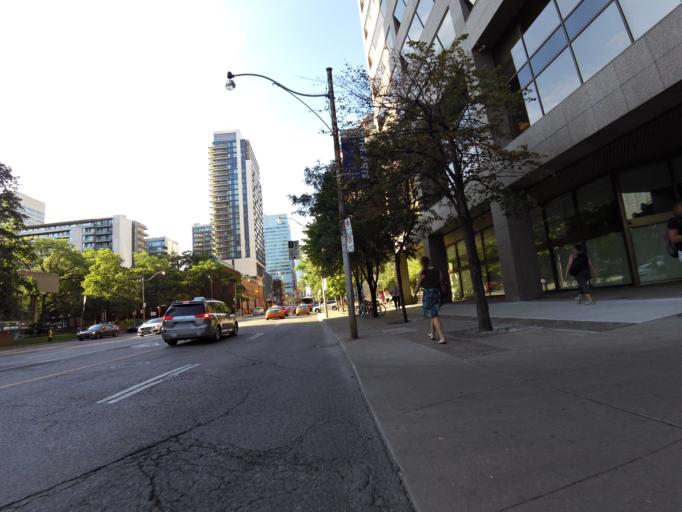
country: CA
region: Ontario
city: Toronto
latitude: 43.6470
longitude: -79.3827
